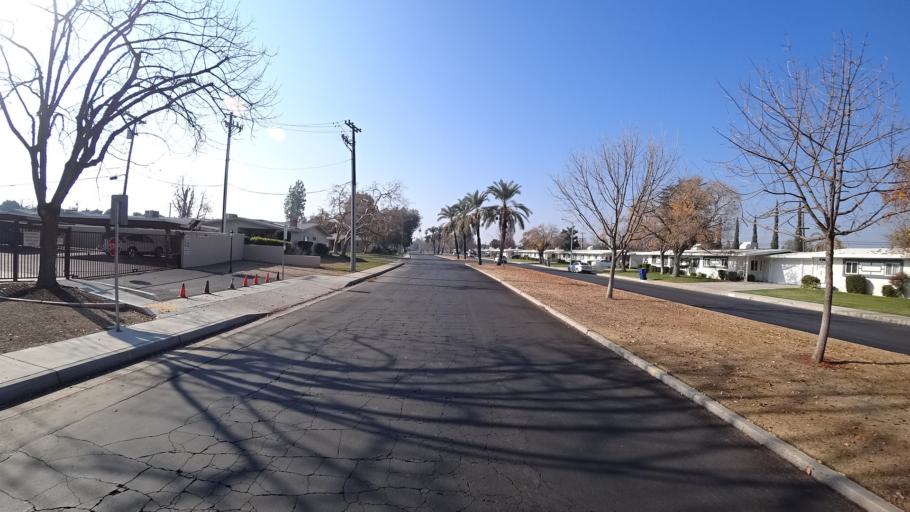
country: US
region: California
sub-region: Kern County
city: Bakersfield
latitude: 35.3442
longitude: -119.0628
